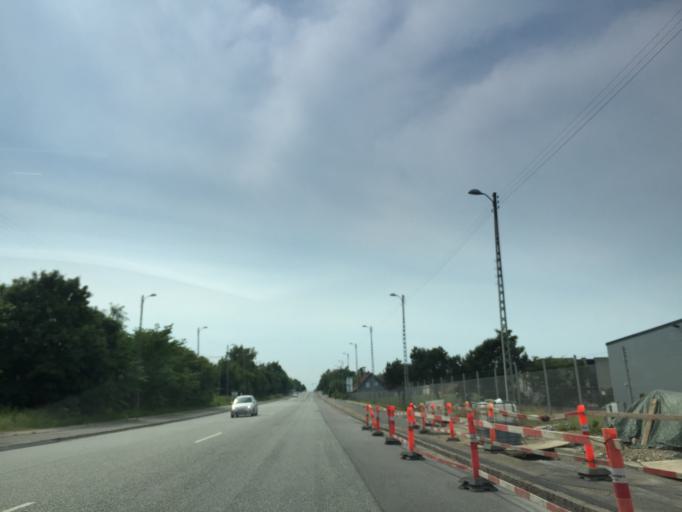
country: DK
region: Capital Region
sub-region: Hoje-Taastrup Kommune
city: Flong
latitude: 55.6483
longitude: 12.1839
